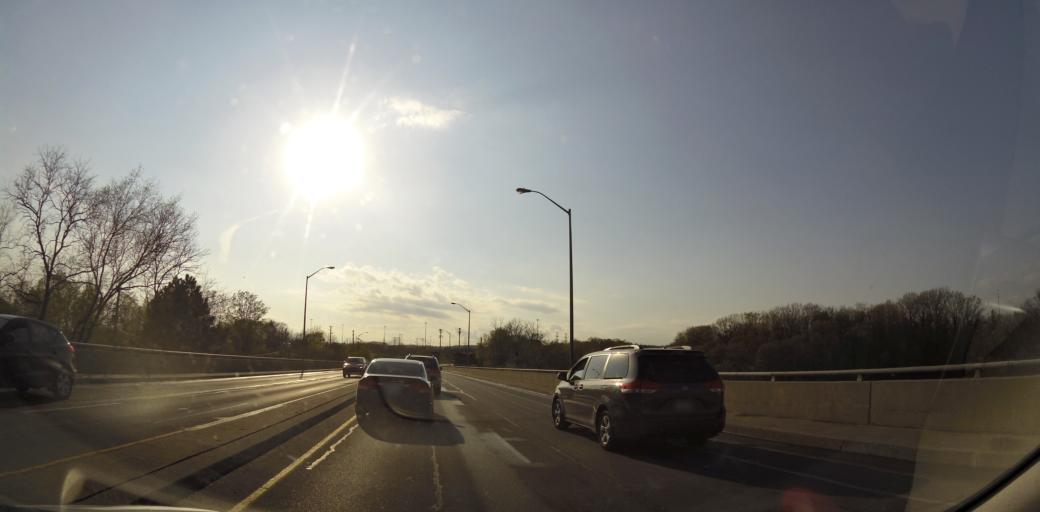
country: CA
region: Ontario
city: Hamilton
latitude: 43.2928
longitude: -79.8849
